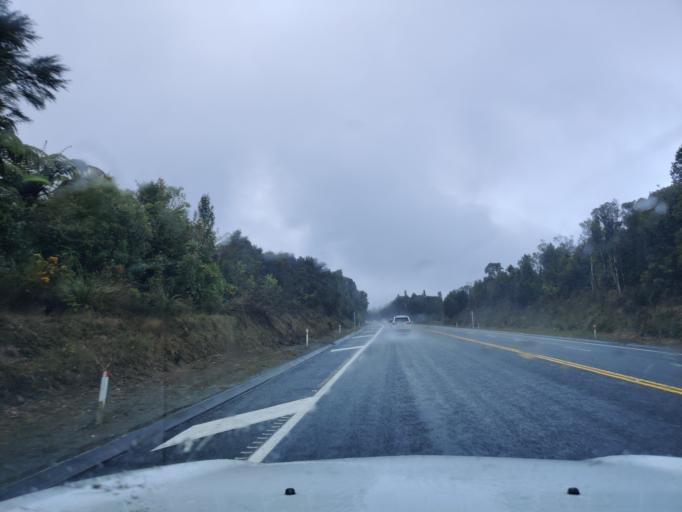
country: NZ
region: Waikato
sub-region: South Waikato District
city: Tokoroa
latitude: -38.0161
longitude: 175.9494
